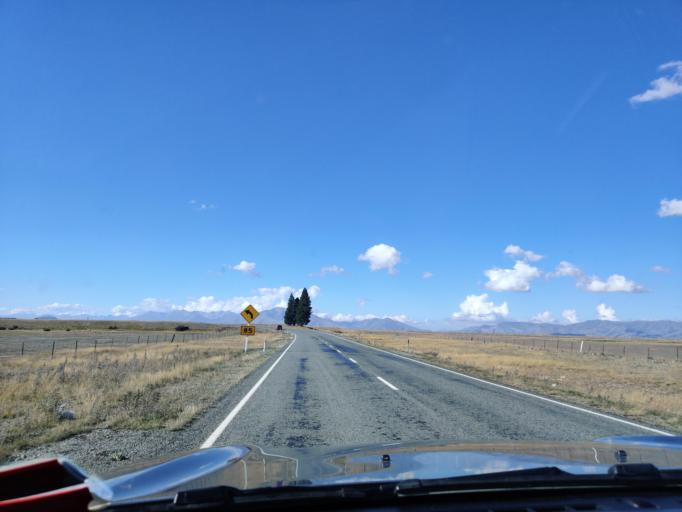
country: NZ
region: Canterbury
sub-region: Timaru District
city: Pleasant Point
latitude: -44.1710
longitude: 170.3301
